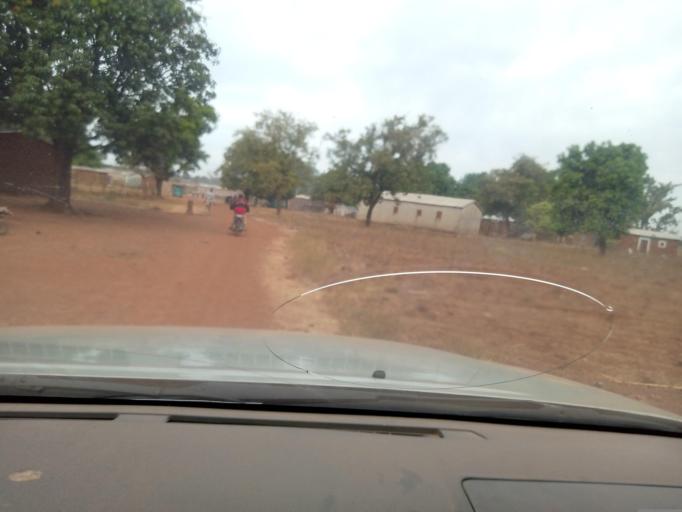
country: ML
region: Sikasso
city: Sikasso
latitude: 11.0210
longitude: -5.7143
